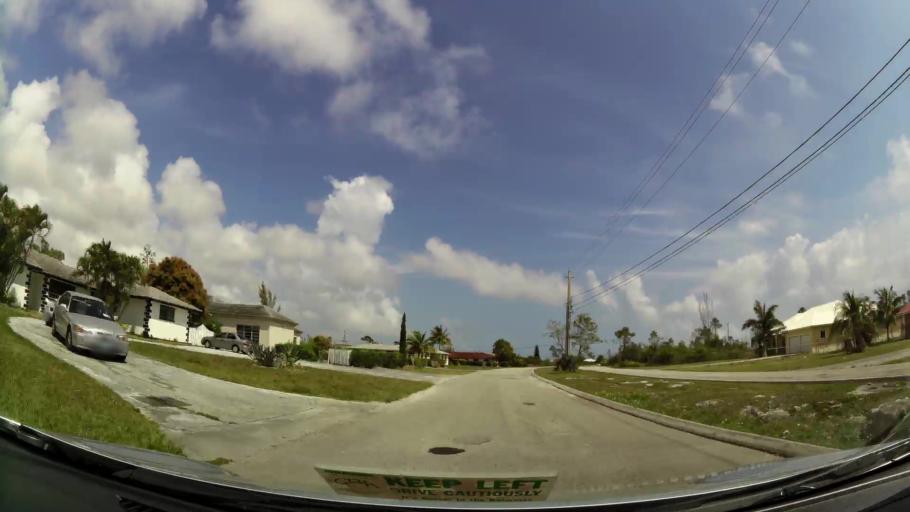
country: BS
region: Freeport
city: Freeport
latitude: 26.5059
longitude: -78.7196
